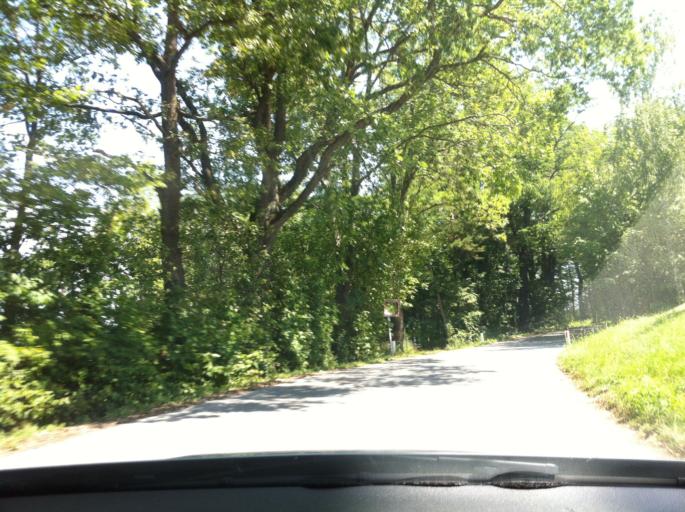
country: AT
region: Styria
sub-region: Politischer Bezirk Weiz
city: Puch bei Weiz
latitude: 47.2297
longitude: 15.7382
